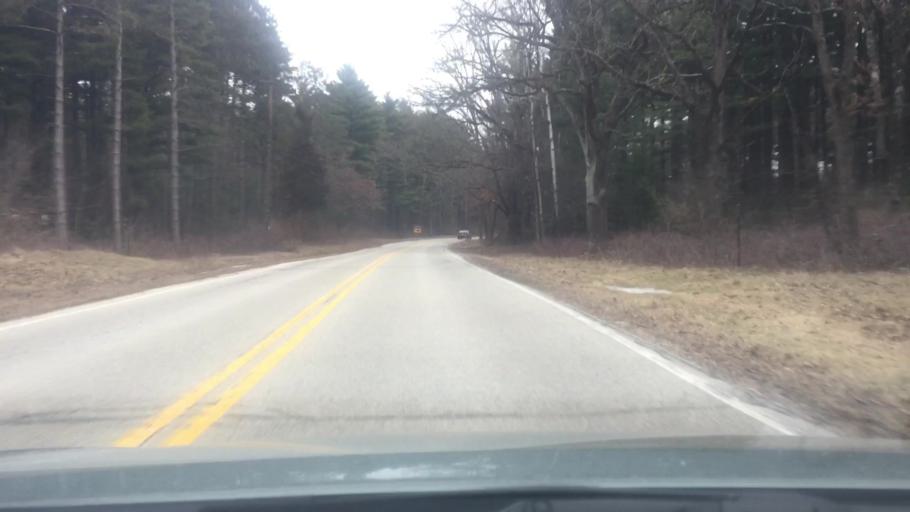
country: US
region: Wisconsin
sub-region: Waukesha County
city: North Prairie
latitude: 42.9424
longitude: -88.4448
